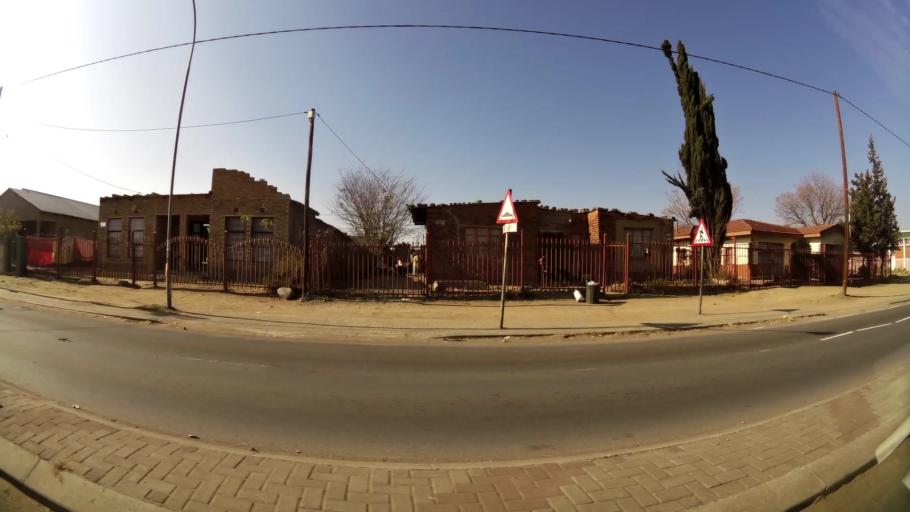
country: ZA
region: Orange Free State
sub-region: Mangaung Metropolitan Municipality
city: Bloemfontein
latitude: -29.1608
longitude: 26.2393
